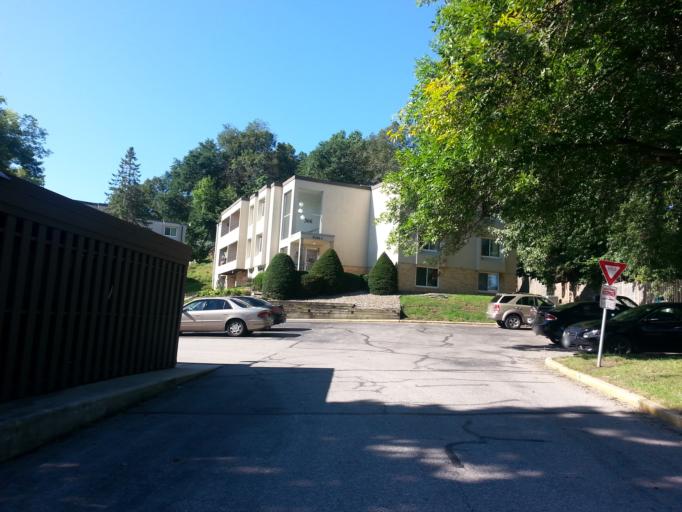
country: US
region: Minnesota
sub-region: Olmsted County
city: Rochester
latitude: 44.0464
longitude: -92.4705
